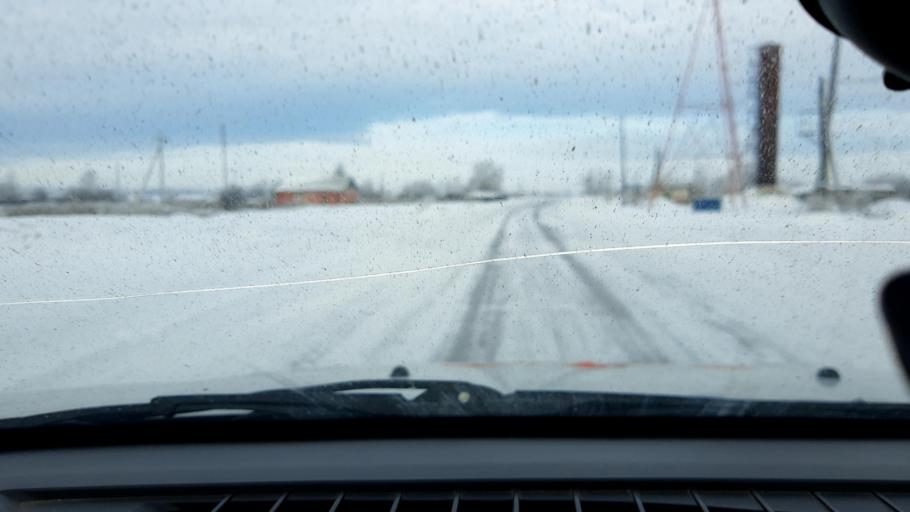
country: RU
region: Nizjnij Novgorod
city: Bogorodsk
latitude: 56.0432
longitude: 43.6294
